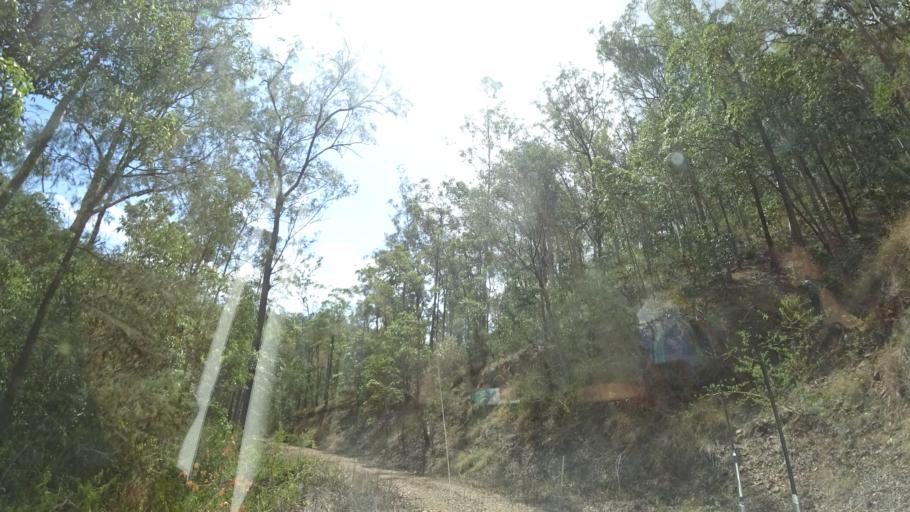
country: AU
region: Queensland
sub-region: Moreton Bay
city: Highvale
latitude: -27.3623
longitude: 152.7289
